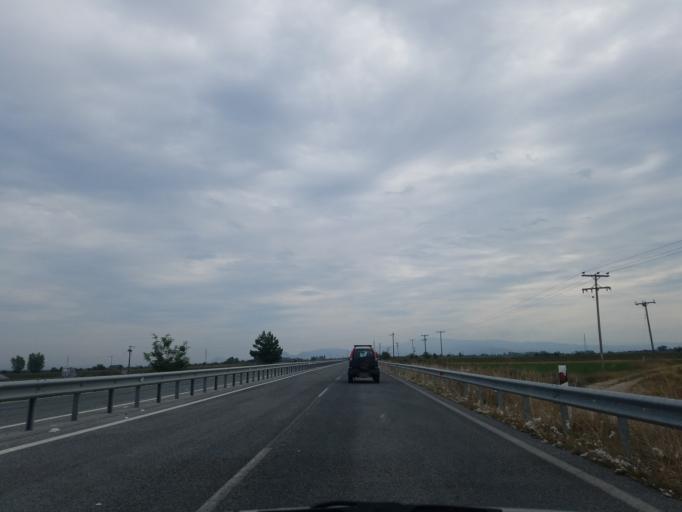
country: GR
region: Thessaly
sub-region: Nomos Kardhitsas
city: Sofades
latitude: 39.3002
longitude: 22.1362
